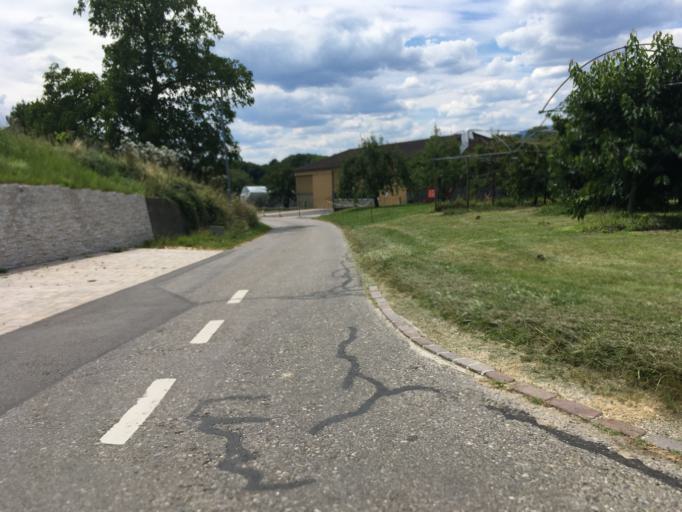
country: CH
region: Fribourg
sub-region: Broye District
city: Estavayer-le-Lac
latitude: 46.8882
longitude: 6.9039
